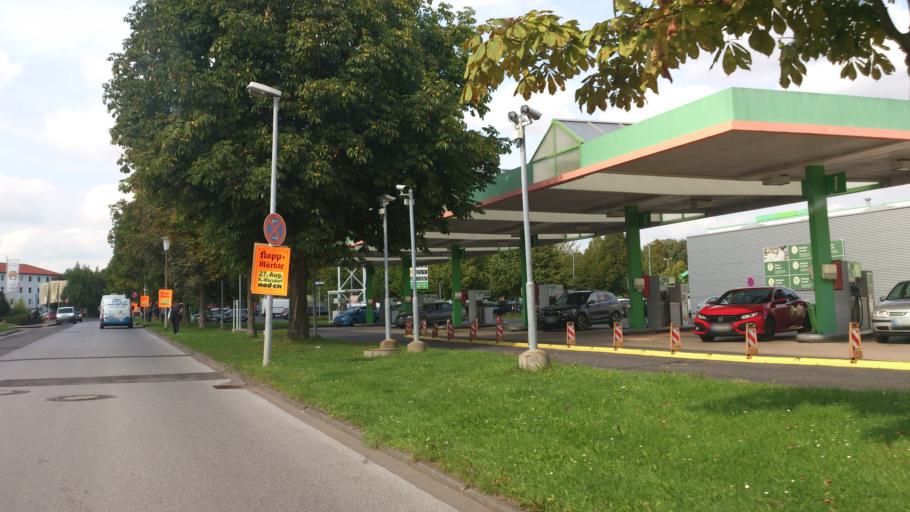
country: DE
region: North Rhine-Westphalia
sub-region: Regierungsbezirk Koln
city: Frechen
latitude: 50.9214
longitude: 6.8517
